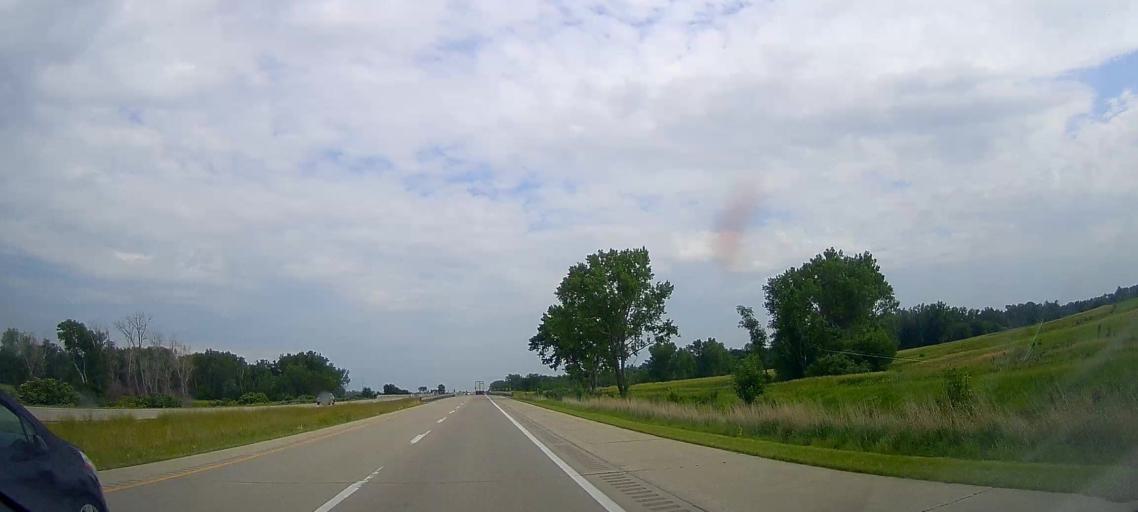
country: US
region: Nebraska
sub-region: Burt County
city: Tekamah
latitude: 41.8222
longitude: -96.0741
